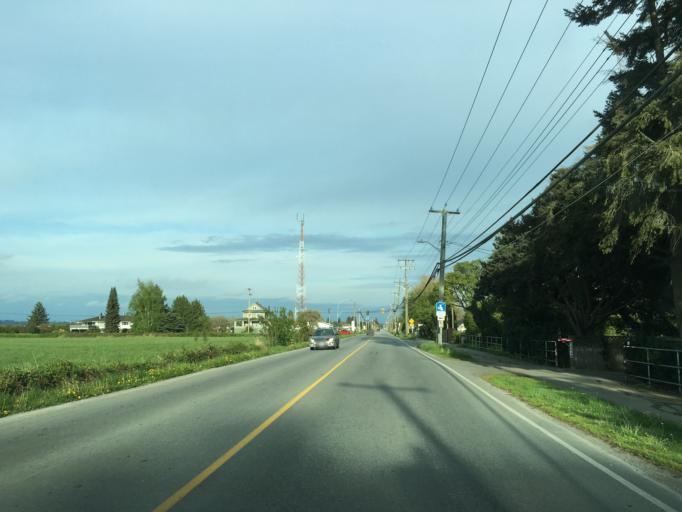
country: CA
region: British Columbia
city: Ladner
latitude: 49.1699
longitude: -123.0489
